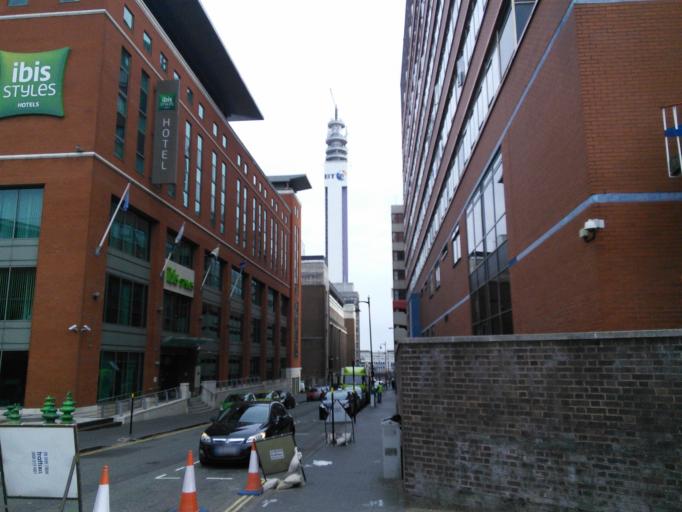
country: GB
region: England
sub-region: City and Borough of Birmingham
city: Birmingham
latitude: 52.4814
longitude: -1.9067
